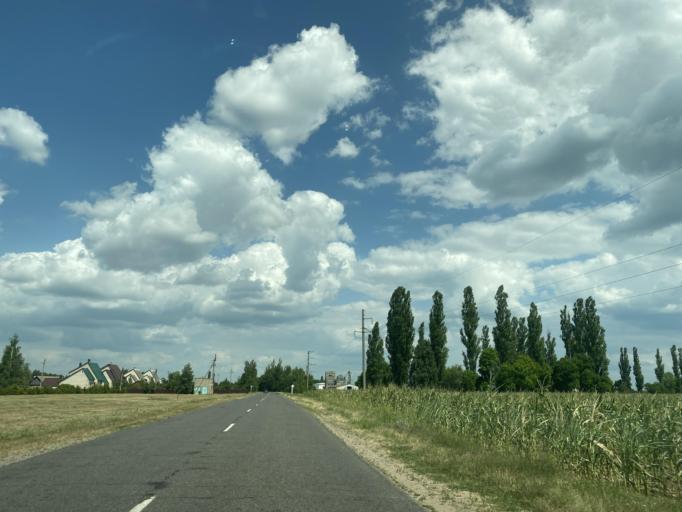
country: BY
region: Brest
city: Ivanava
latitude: 52.3460
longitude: 25.6278
